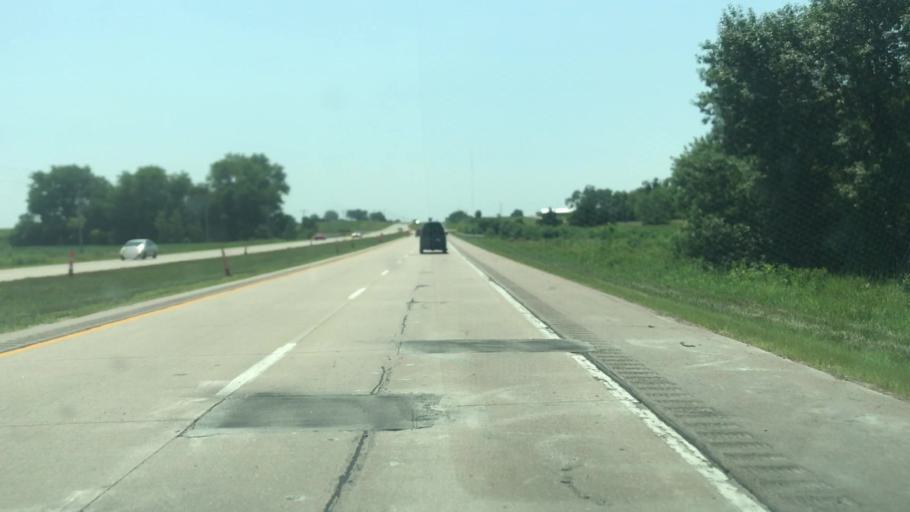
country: US
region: Nebraska
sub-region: Adams County
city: Hastings
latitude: 40.6732
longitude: -98.3823
